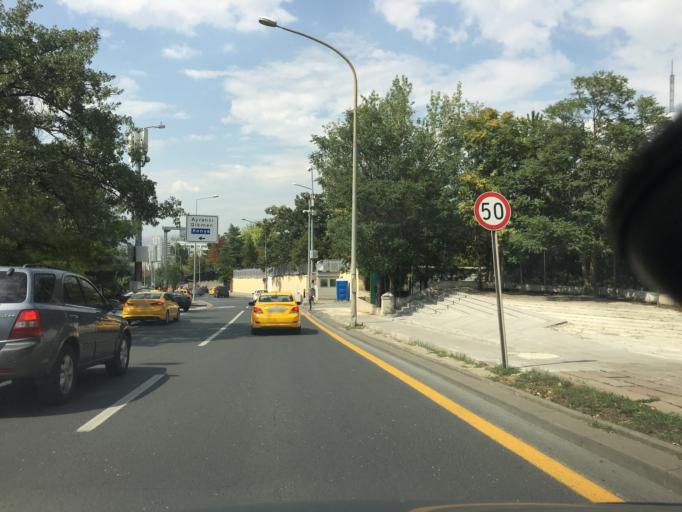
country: TR
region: Ankara
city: Cankaya
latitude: 39.8962
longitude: 32.8619
